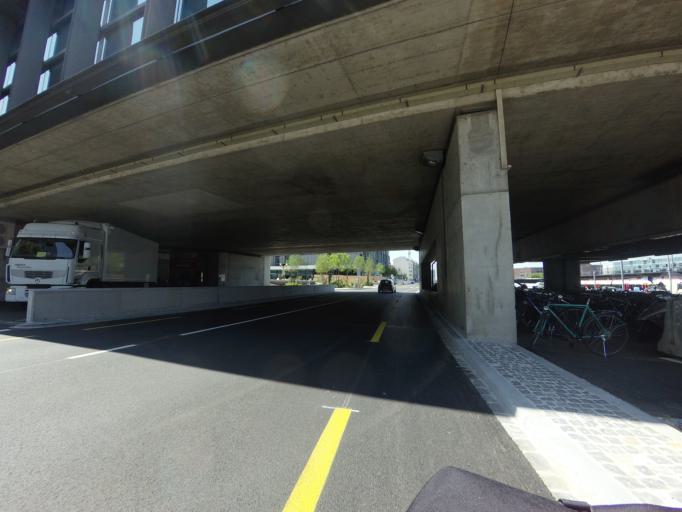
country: CH
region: Basel-City
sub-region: Basel-Stadt
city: Basel
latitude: 47.5460
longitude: 7.5884
